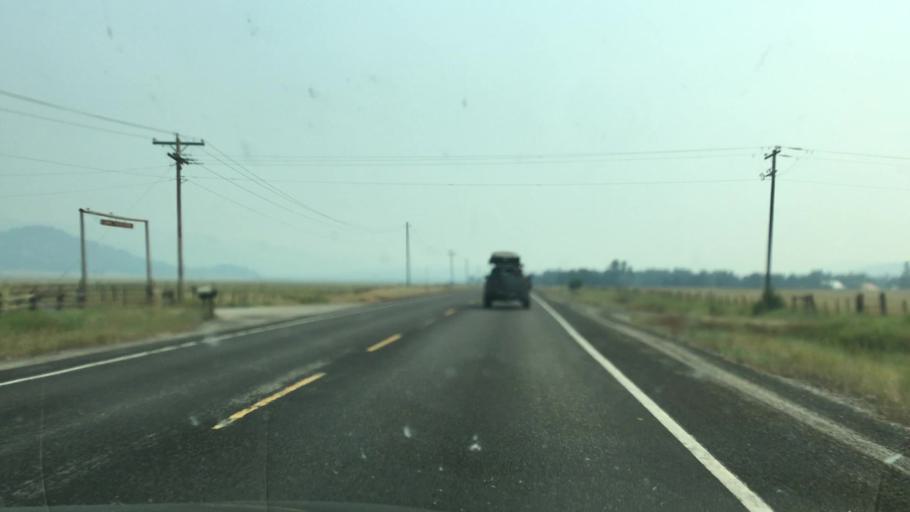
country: US
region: Idaho
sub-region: Valley County
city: Cascade
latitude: 44.4443
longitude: -115.9995
